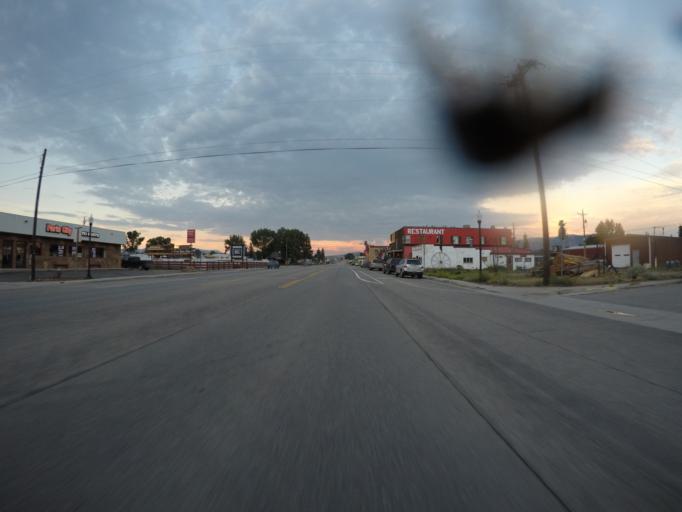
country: US
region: Colorado
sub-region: Grand County
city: Kremmling
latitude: 40.0589
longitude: -106.3948
